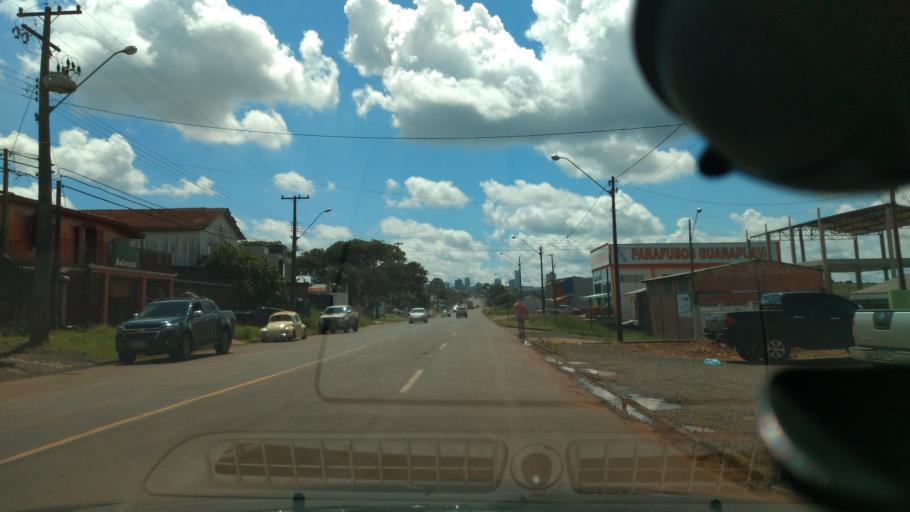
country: BR
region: Parana
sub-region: Guarapuava
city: Guarapuava
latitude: -25.3930
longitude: -51.4963
